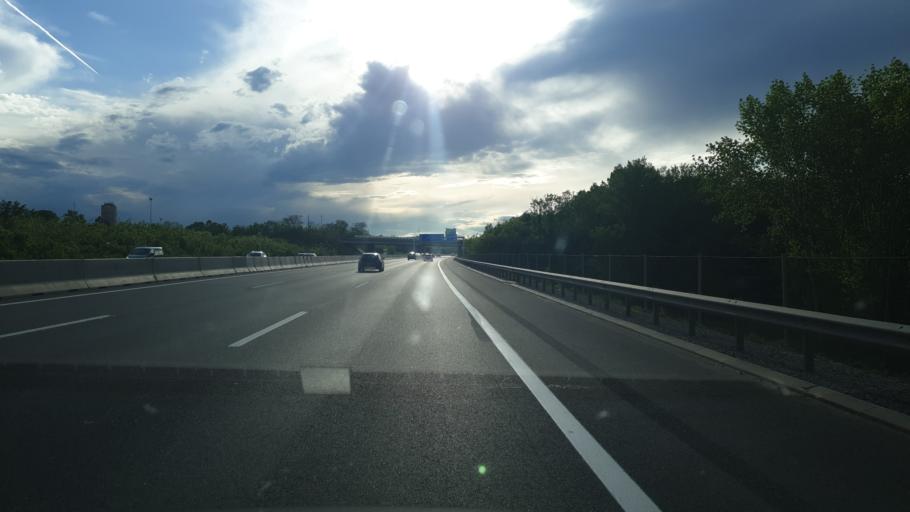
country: AT
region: Lower Austria
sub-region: Politischer Bezirk Wien-Umgebung
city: Fischamend Dorf
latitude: 48.1293
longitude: 16.5557
